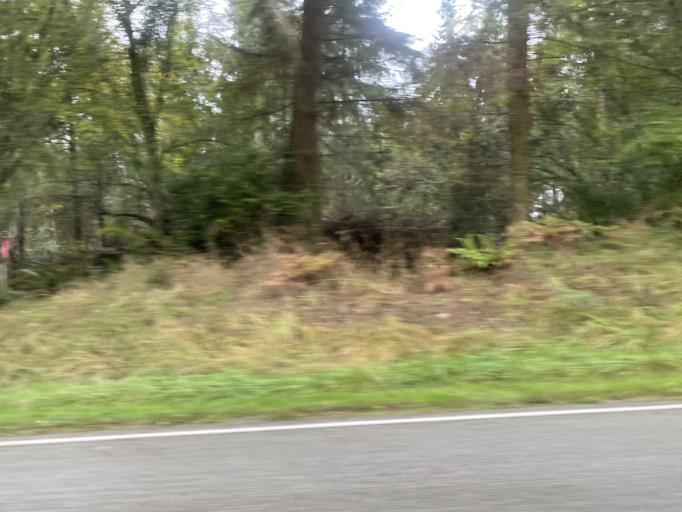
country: US
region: Washington
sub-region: Island County
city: Freeland
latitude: 48.0916
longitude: -122.5049
